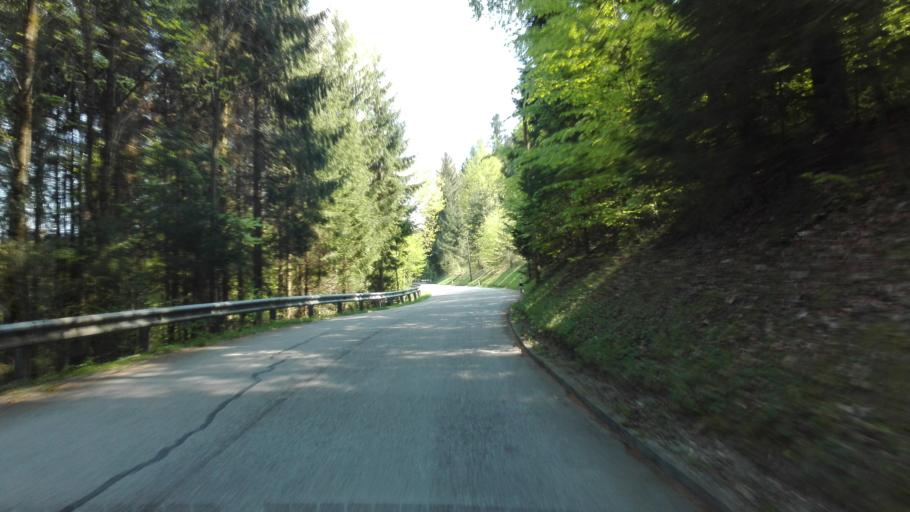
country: AT
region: Upper Austria
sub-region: Politischer Bezirk Rohrbach
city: Atzesberg
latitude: 48.4337
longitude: 13.9166
